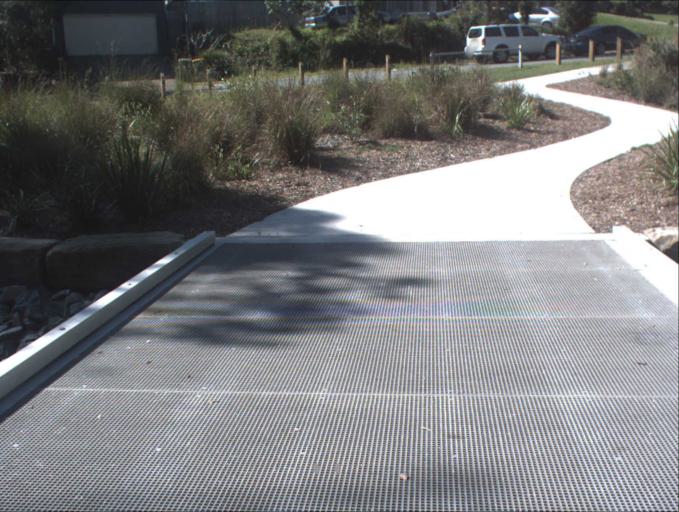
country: AU
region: Queensland
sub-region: Logan
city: Waterford West
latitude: -27.7142
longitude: 153.1533
